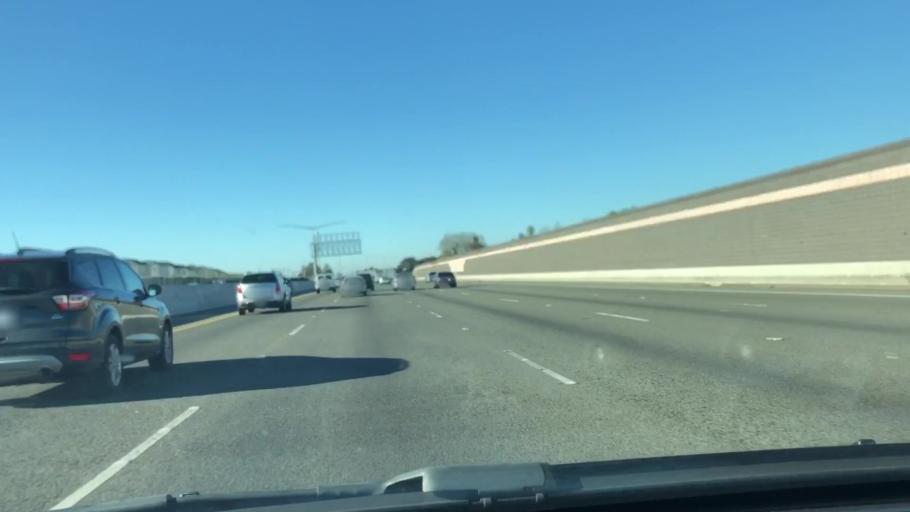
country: US
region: California
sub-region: Alameda County
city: Fremont
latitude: 37.5345
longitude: -122.0107
